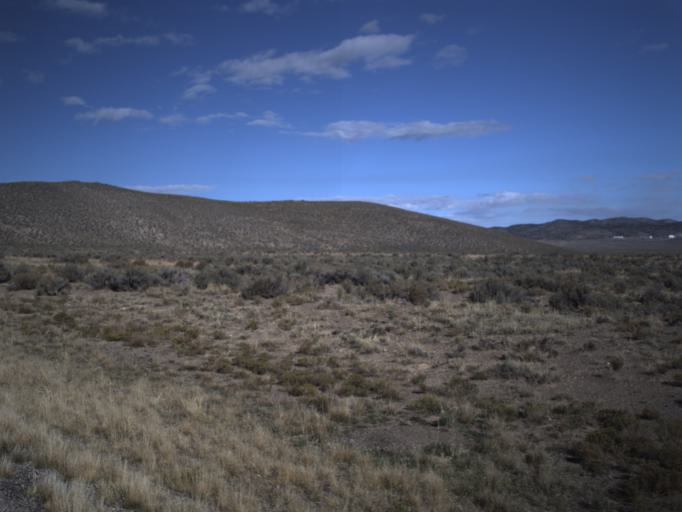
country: US
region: Utah
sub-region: Beaver County
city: Milford
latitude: 38.4232
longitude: -113.1080
